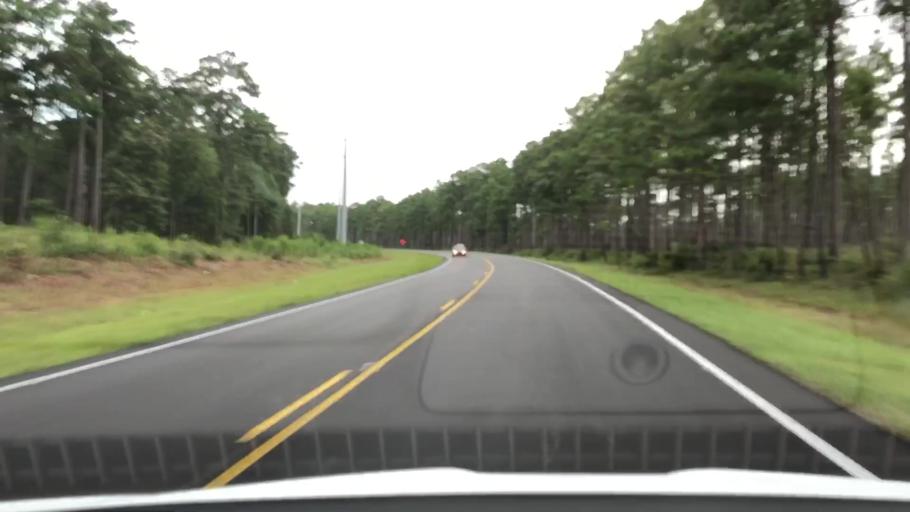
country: US
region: North Carolina
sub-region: Onslow County
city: Swansboro
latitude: 34.7715
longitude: -77.0975
